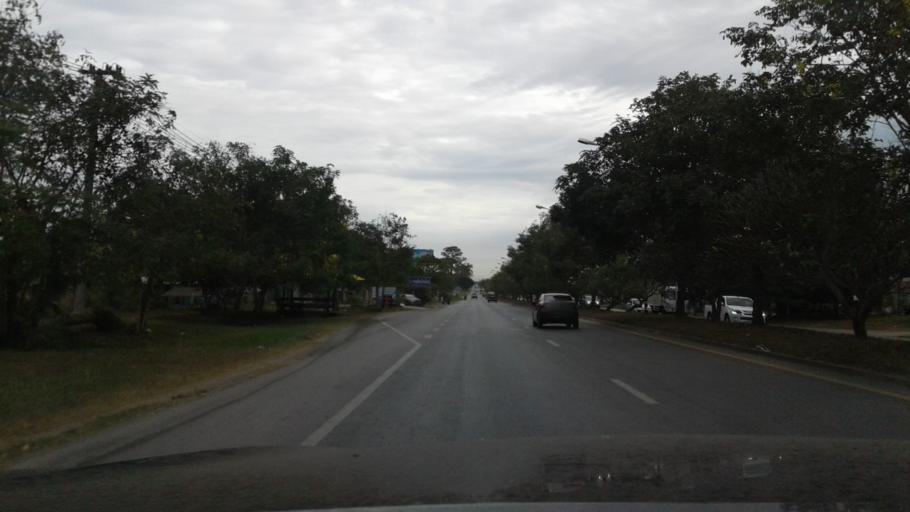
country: TH
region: Changwat Udon Thani
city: Udon Thani
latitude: 17.3629
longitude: 102.7005
